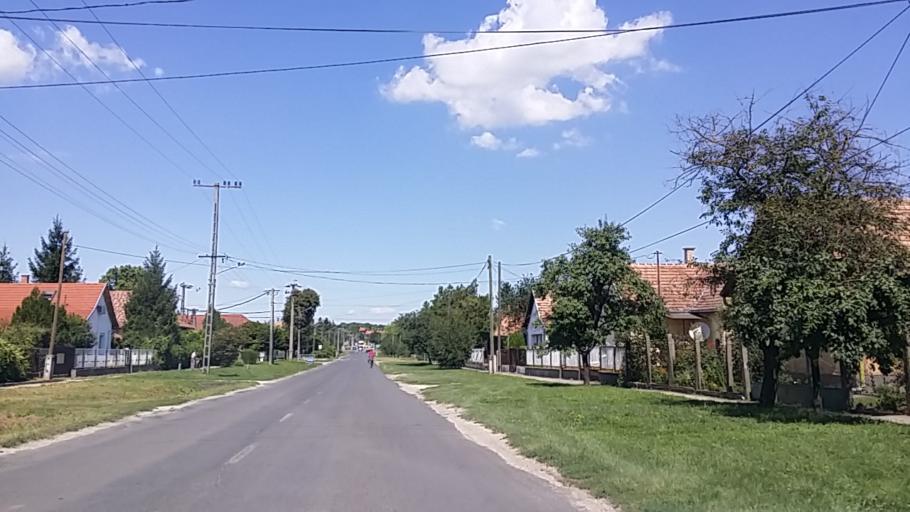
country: HU
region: Tolna
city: Simontornya
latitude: 46.7541
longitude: 18.5455
